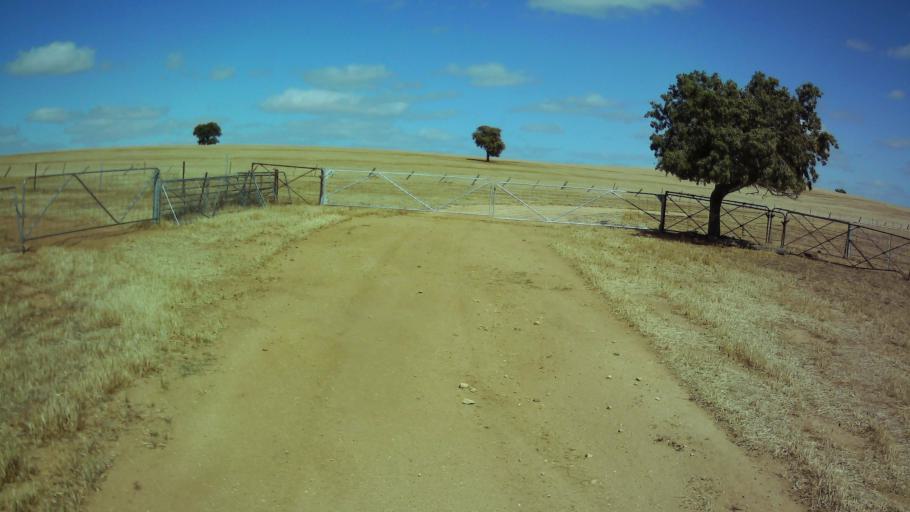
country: AU
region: New South Wales
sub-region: Weddin
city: Grenfell
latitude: -33.9794
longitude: 148.3838
